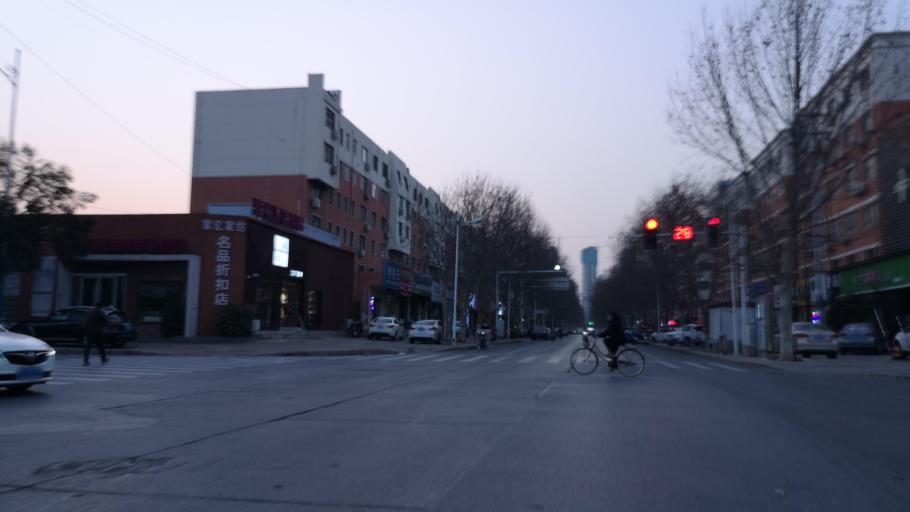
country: CN
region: Henan Sheng
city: Zhongyuanlu
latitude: 35.7665
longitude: 115.0633
